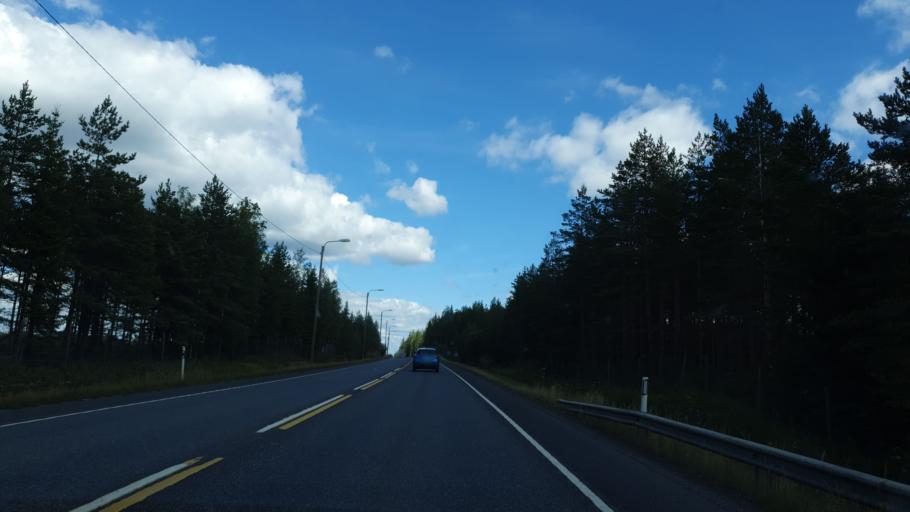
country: FI
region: Pirkanmaa
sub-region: Tampere
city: Orivesi
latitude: 61.6511
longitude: 24.2383
